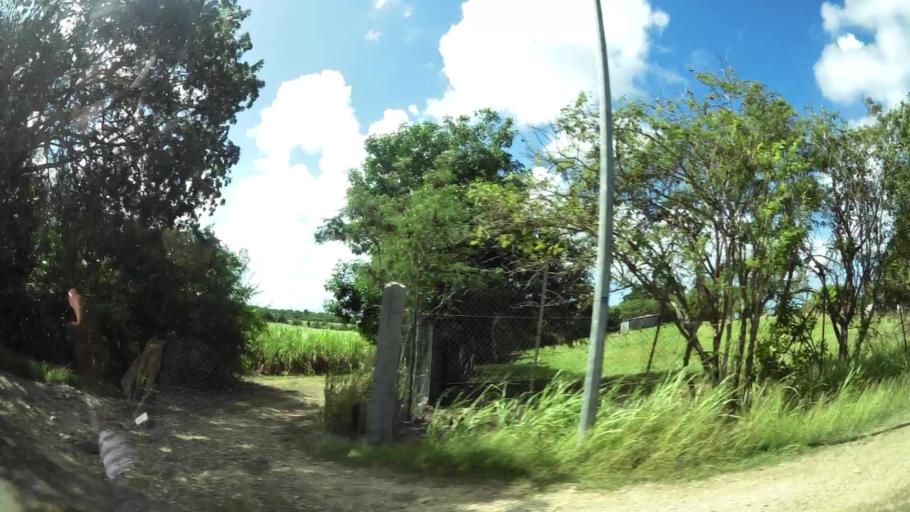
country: GP
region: Guadeloupe
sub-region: Guadeloupe
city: Anse-Bertrand
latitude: 16.4628
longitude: -61.4863
